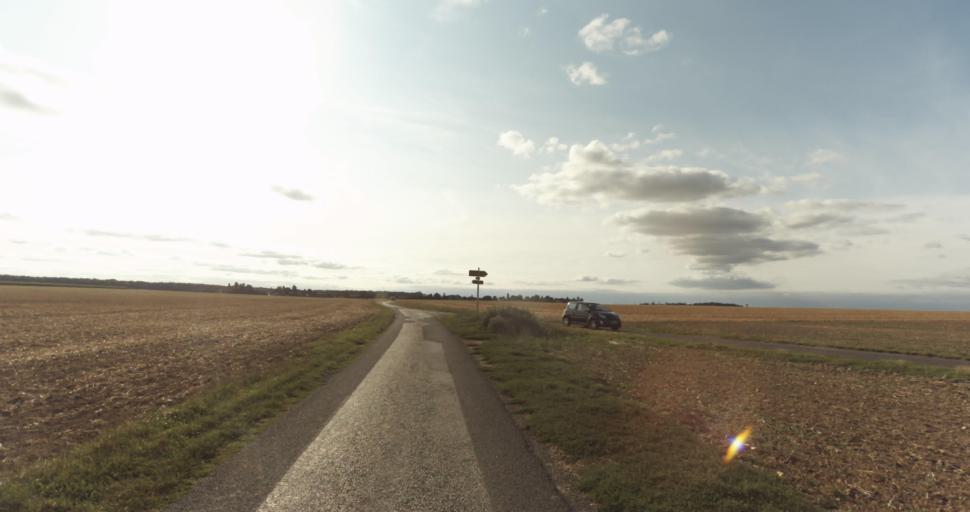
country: FR
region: Haute-Normandie
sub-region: Departement de l'Eure
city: La Couture-Boussey
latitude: 48.9051
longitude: 1.3280
